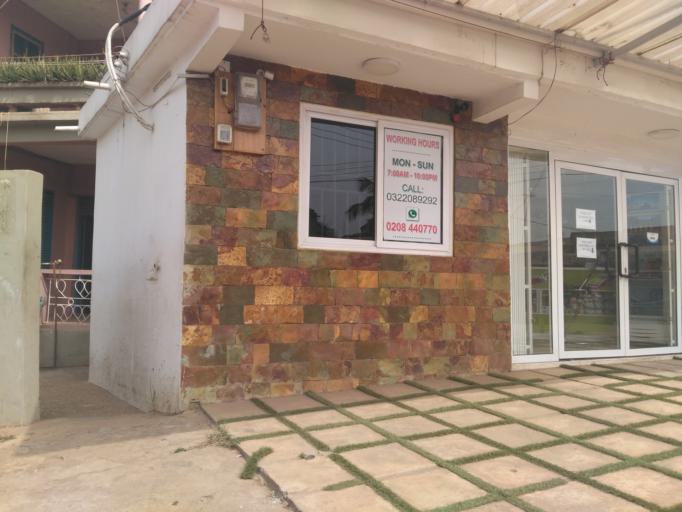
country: GH
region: Ashanti
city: Kumasi
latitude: 6.6830
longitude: -1.6021
